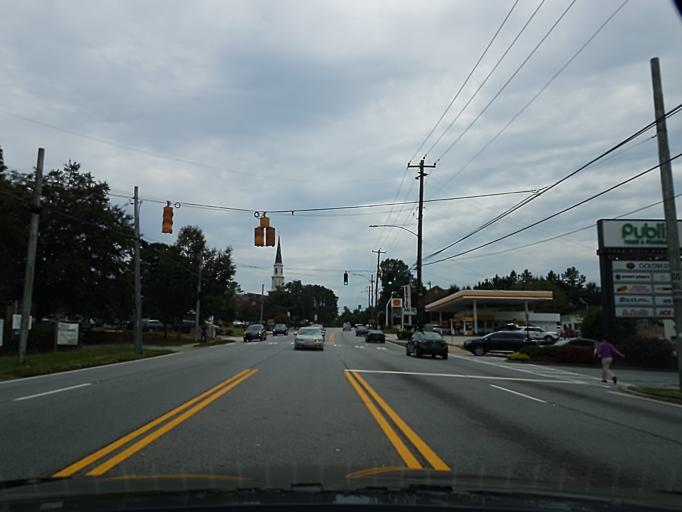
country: US
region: Georgia
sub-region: DeKalb County
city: North Druid Hills
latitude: 33.8149
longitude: -84.3098
